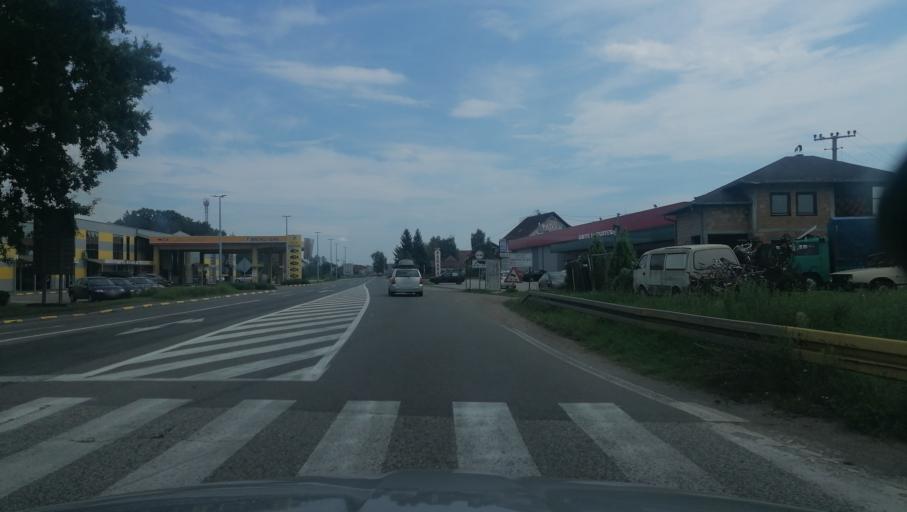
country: BA
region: Republika Srpska
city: Obudovac
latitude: 44.9410
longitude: 18.6778
